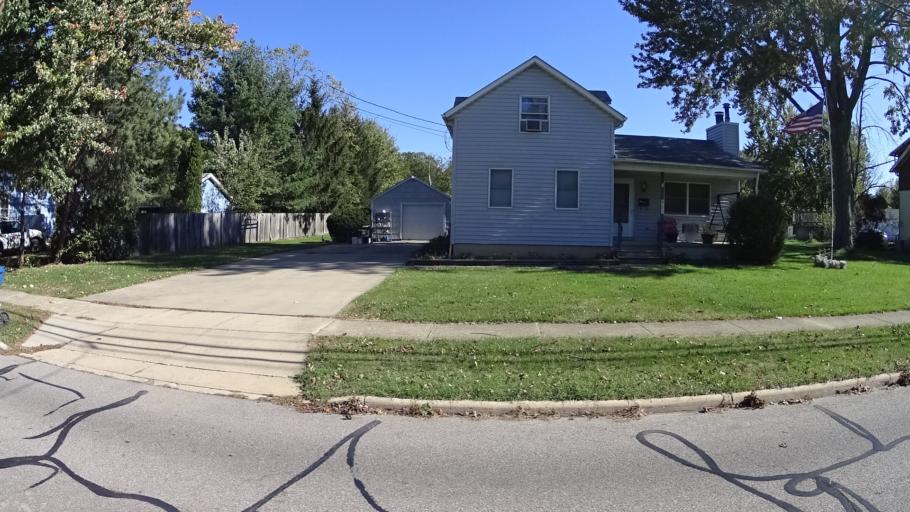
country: US
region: Ohio
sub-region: Lorain County
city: Amherst
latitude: 41.3970
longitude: -82.2175
